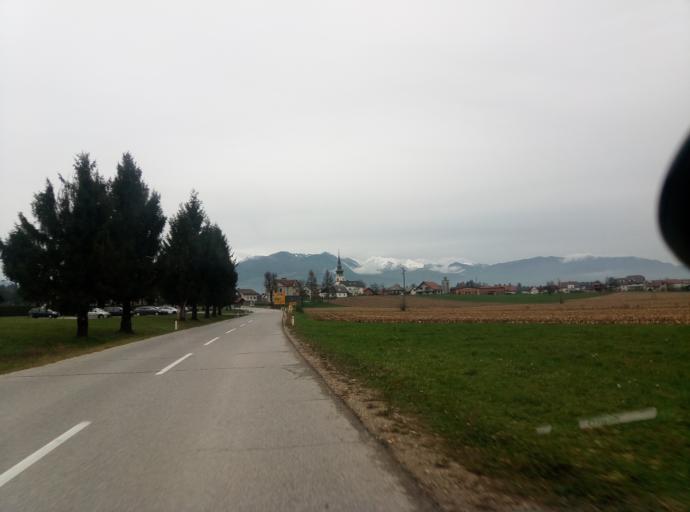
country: SI
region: Vodice
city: Vodice
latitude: 46.1836
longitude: 14.4896
